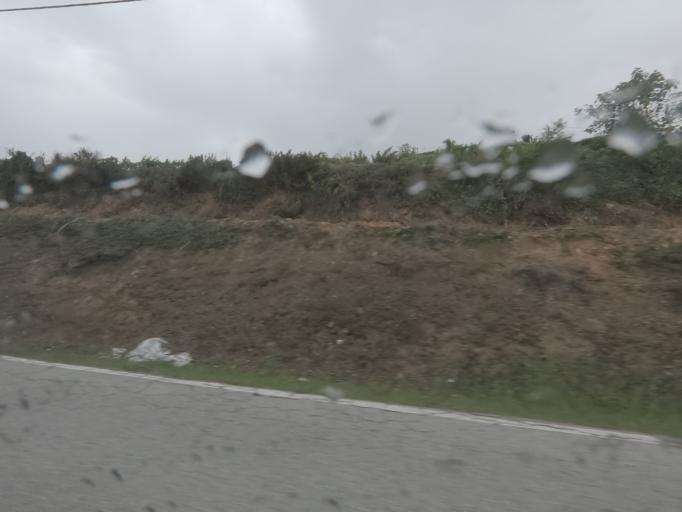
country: PT
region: Viseu
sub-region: Armamar
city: Armamar
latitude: 41.1157
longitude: -7.7198
